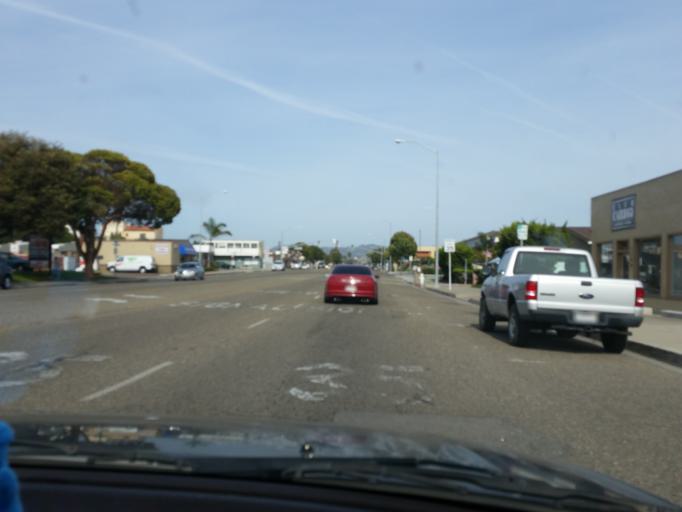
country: US
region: California
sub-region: San Luis Obispo County
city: Grover Beach
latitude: 35.1213
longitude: -120.6174
